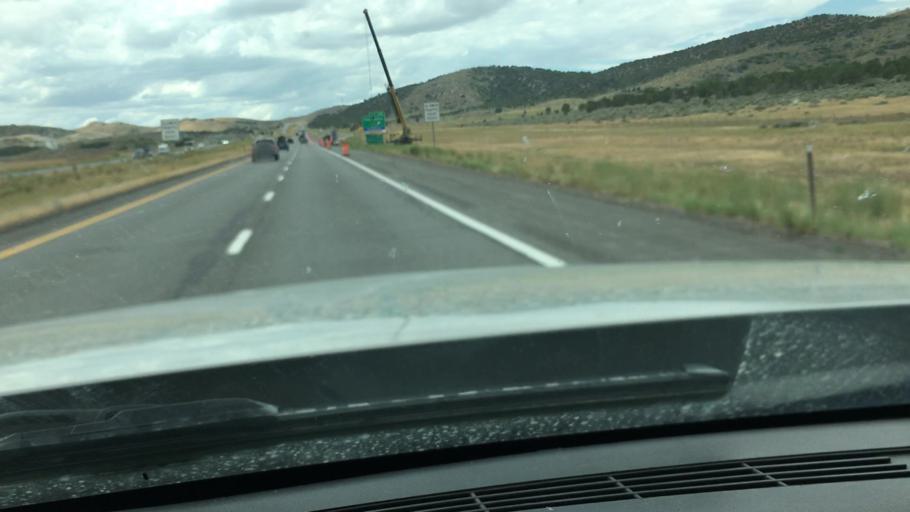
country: US
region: Utah
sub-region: Beaver County
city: Beaver
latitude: 38.6644
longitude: -112.5911
